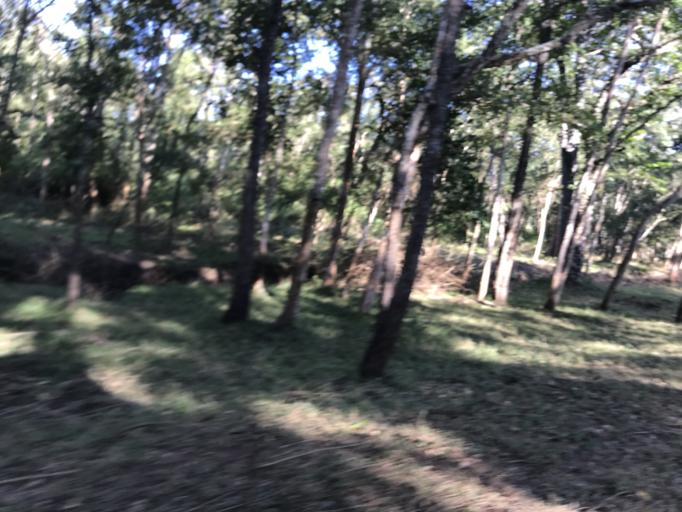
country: IN
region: Karnataka
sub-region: Mysore
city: Heggadadevankote
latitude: 11.9798
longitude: 76.2337
